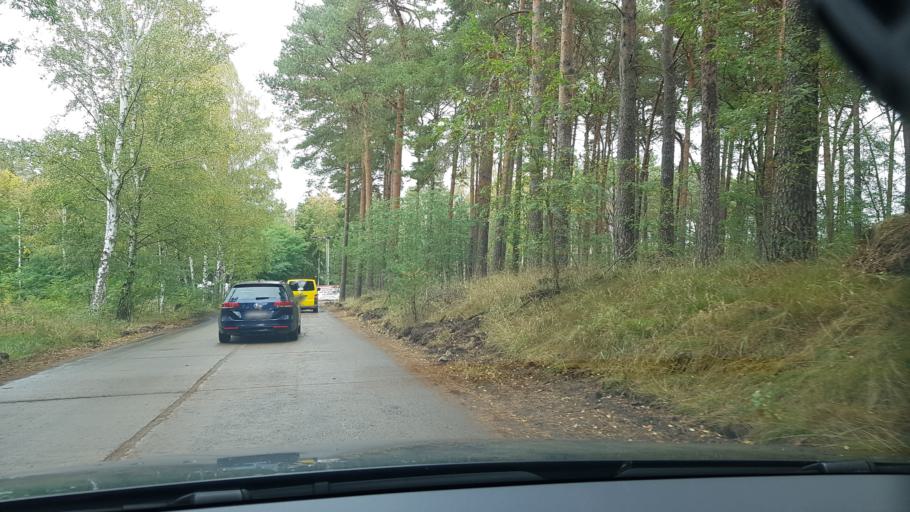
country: DE
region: Saxony-Anhalt
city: Tangerhutte
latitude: 52.3784
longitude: 11.8263
